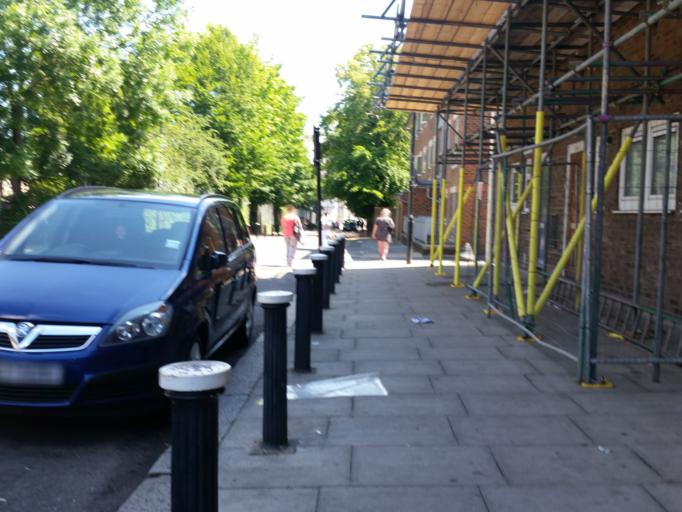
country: GB
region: England
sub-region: Greater London
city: Harringay
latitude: 51.6023
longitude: -0.0700
